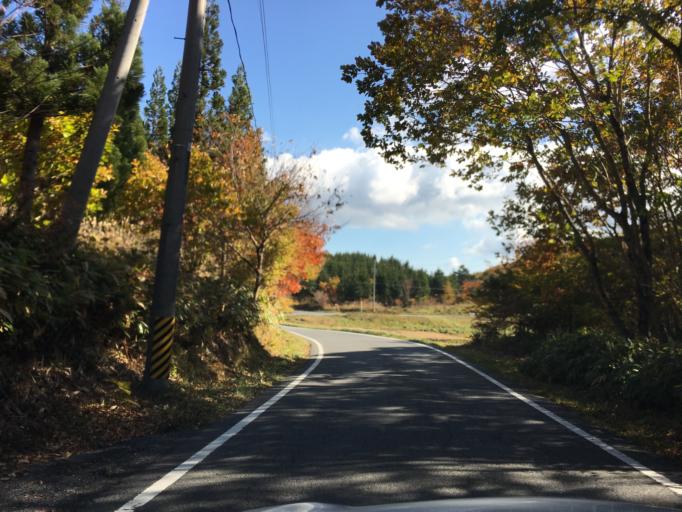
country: JP
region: Fukushima
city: Funehikimachi-funehiki
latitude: 37.2937
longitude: 140.7372
